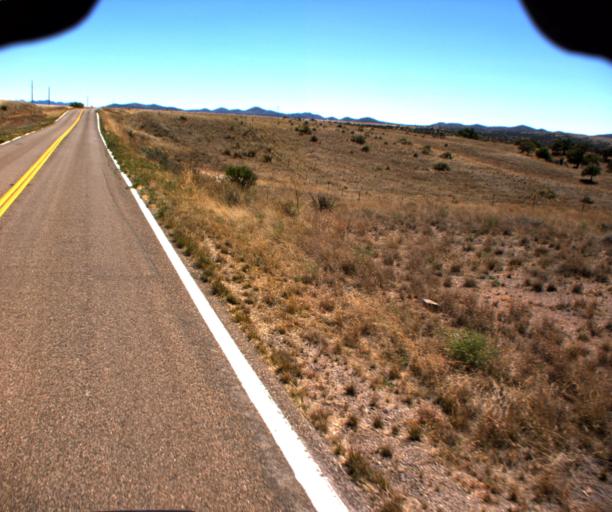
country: US
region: Arizona
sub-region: Cochise County
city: Huachuca City
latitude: 31.6524
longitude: -110.6044
